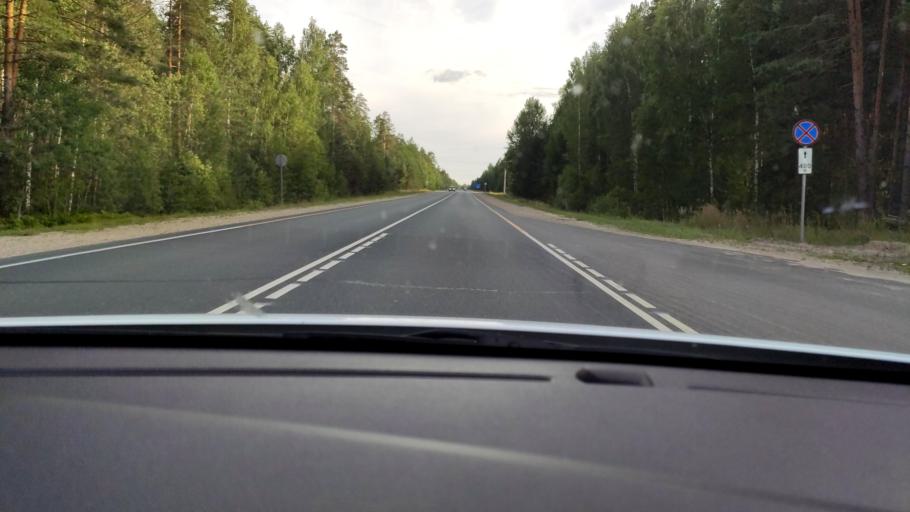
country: RU
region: Mariy-El
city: Suslonger
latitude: 56.2523
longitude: 48.2324
